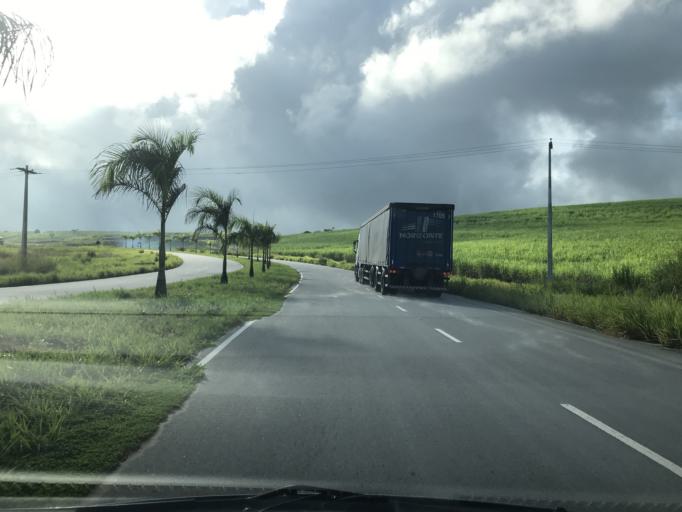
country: BR
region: Pernambuco
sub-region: Itapissuma
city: Itapissuma
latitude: -7.7661
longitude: -34.9340
